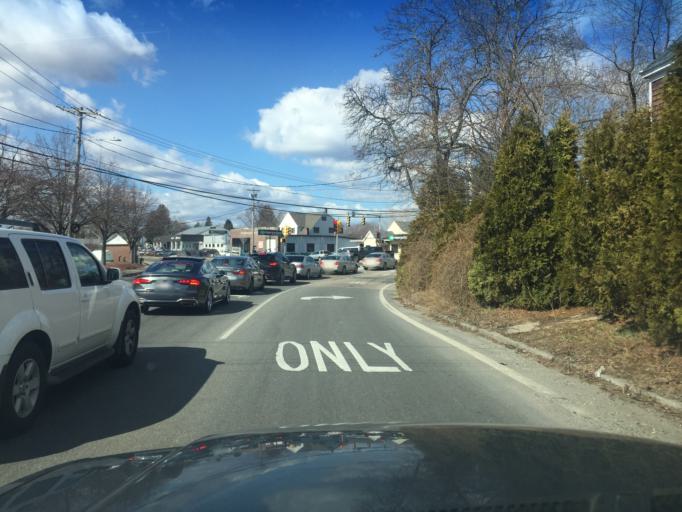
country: US
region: Massachusetts
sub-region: Worcester County
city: Milford
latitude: 42.1504
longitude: -71.5030
